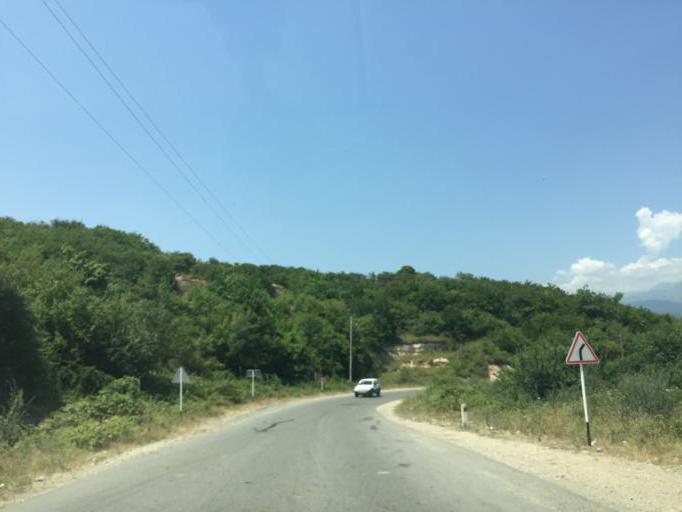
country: AZ
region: Tartar Rayon
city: Martakert
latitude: 40.1399
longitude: 46.5854
